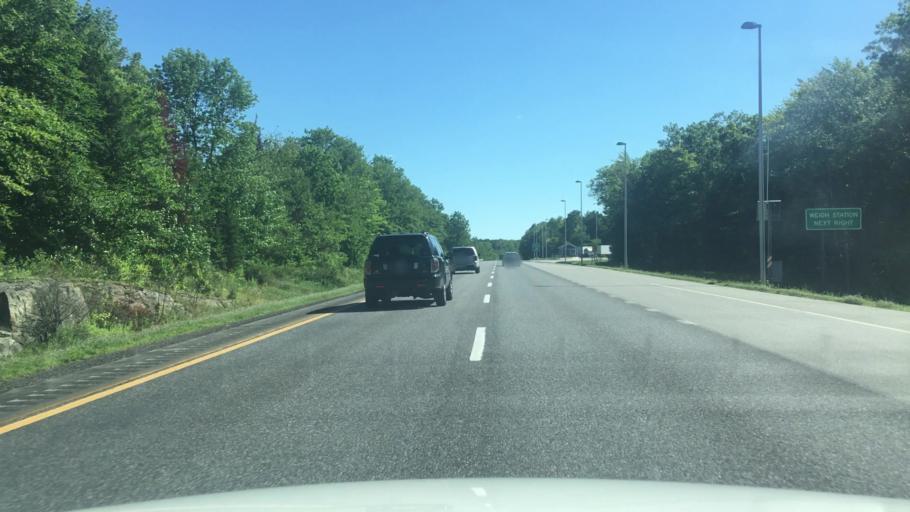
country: US
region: Maine
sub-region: Kennebec County
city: Sidney
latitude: 44.4059
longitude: -69.7502
